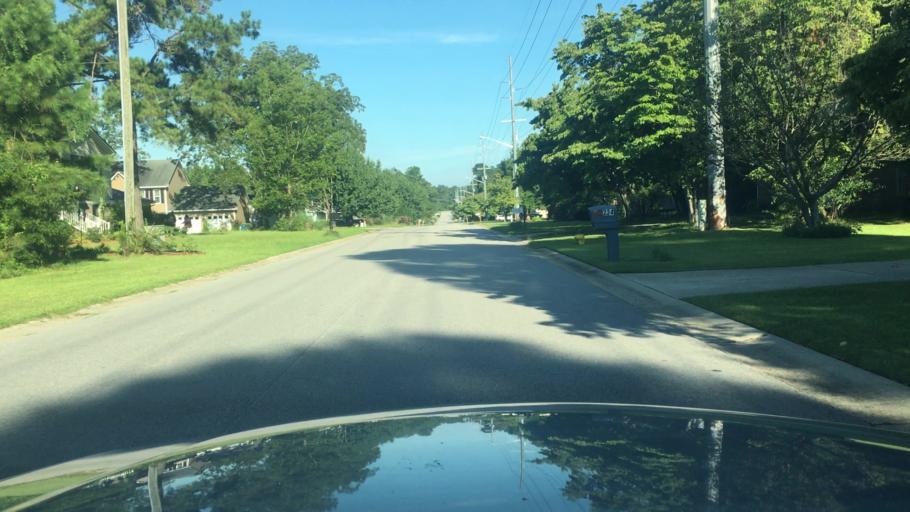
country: US
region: North Carolina
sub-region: Cumberland County
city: Fayetteville
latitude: 35.1292
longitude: -78.8836
